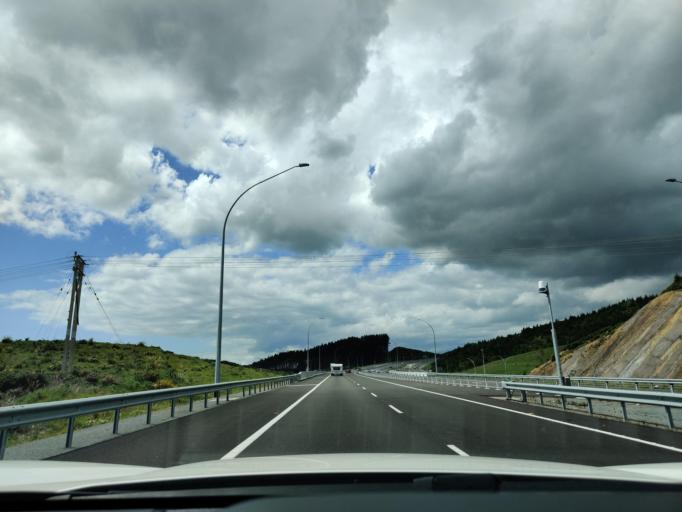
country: NZ
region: Wellington
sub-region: Porirua City
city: Porirua
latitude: -41.1528
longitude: 174.8423
